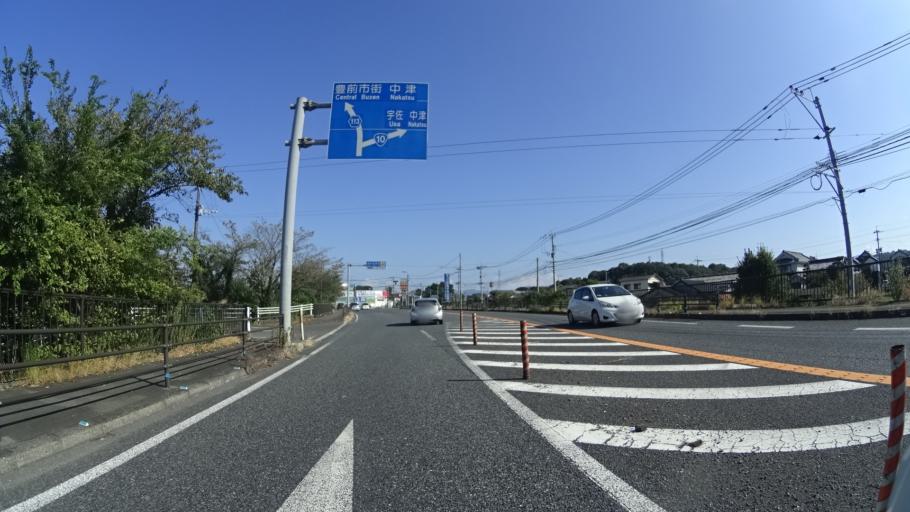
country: JP
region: Fukuoka
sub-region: Buzen-shi
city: Buzen
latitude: 33.6170
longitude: 131.0983
